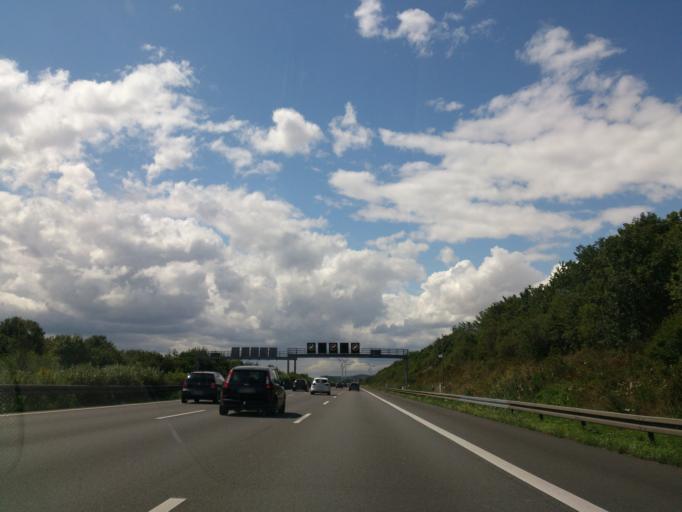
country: DE
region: Lower Saxony
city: Gross Munzel
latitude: 52.3790
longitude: 9.4622
